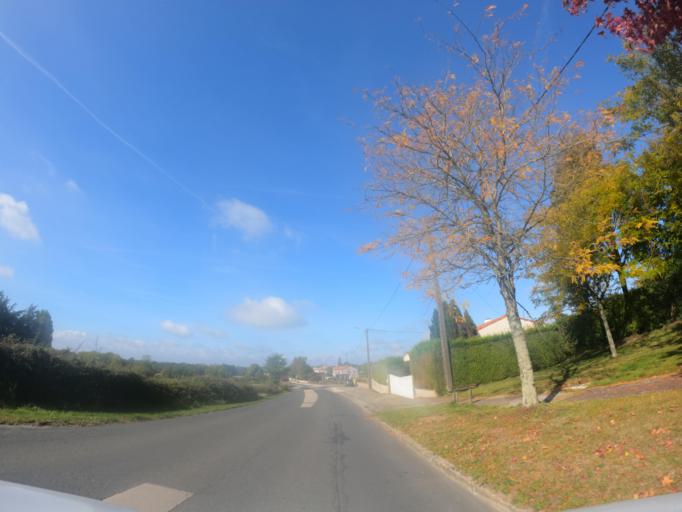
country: FR
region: Poitou-Charentes
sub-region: Departement des Deux-Sevres
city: Courlay
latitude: 46.7816
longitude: -0.5692
